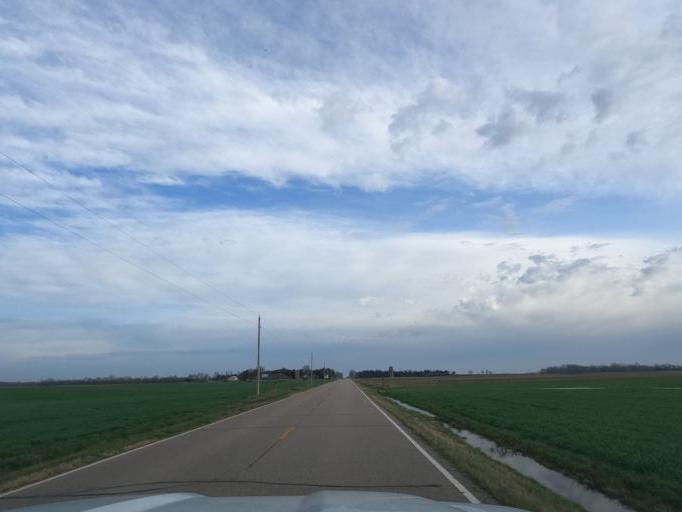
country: US
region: Kansas
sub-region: Reno County
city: Nickerson
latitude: 38.0062
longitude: -98.1788
